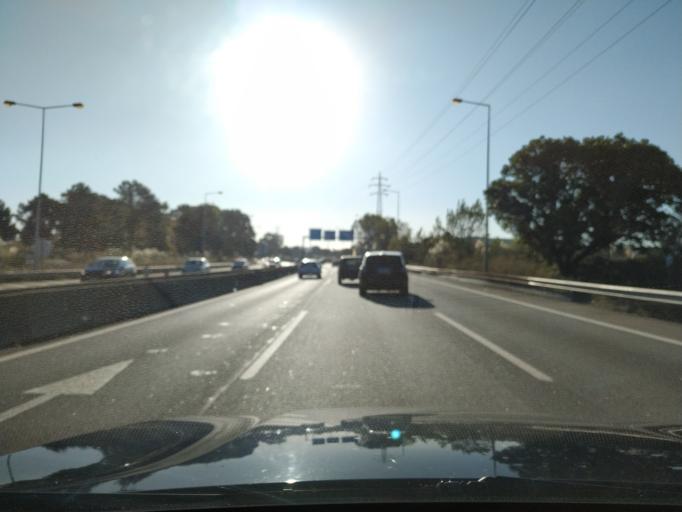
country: PT
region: Porto
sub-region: Vila Nova de Gaia
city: Canidelo
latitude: 41.1177
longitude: -8.6323
